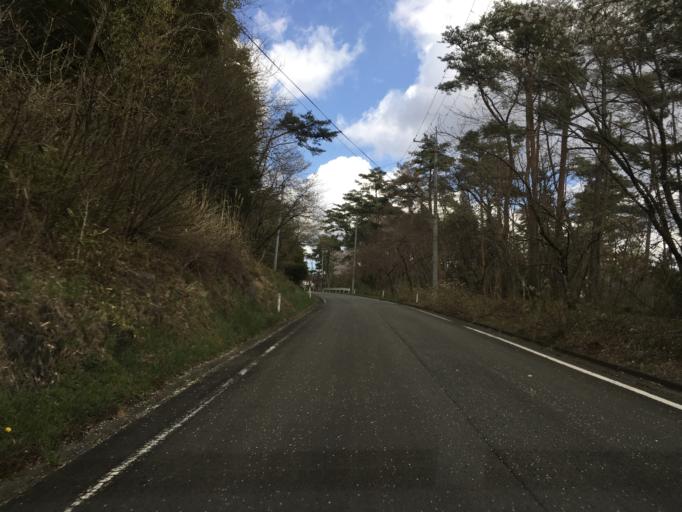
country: JP
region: Iwate
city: Ichinoseki
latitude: 38.7493
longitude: 141.2699
